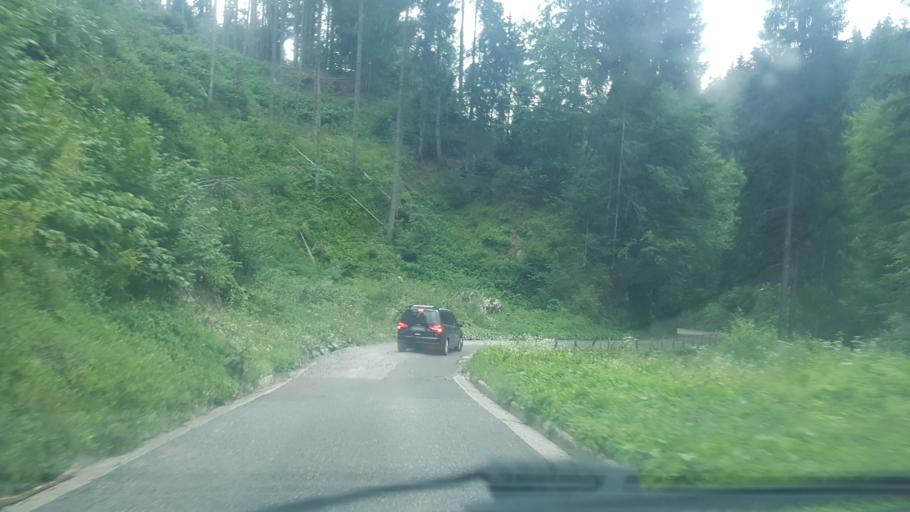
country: IT
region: Friuli Venezia Giulia
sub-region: Provincia di Udine
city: Rigolato
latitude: 46.5520
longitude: 12.8317
